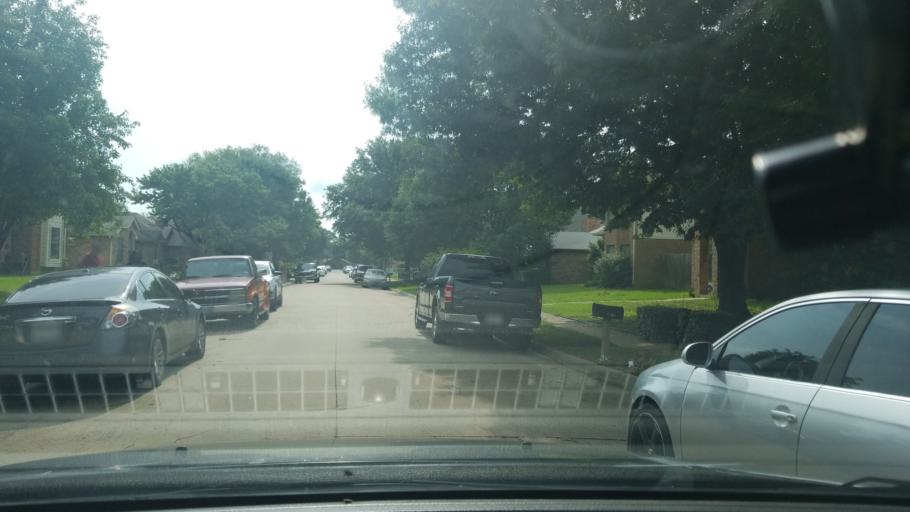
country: US
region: Texas
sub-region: Dallas County
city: Balch Springs
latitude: 32.7559
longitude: -96.6282
